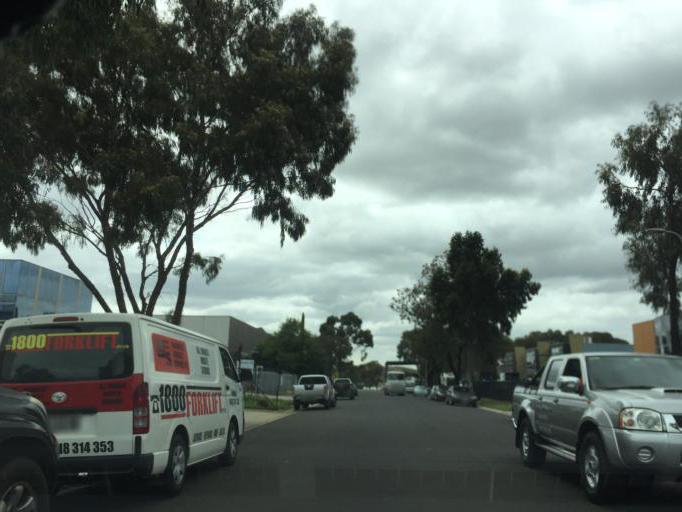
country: AU
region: Victoria
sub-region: Brimbank
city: Brooklyn
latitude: -37.8206
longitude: 144.8223
